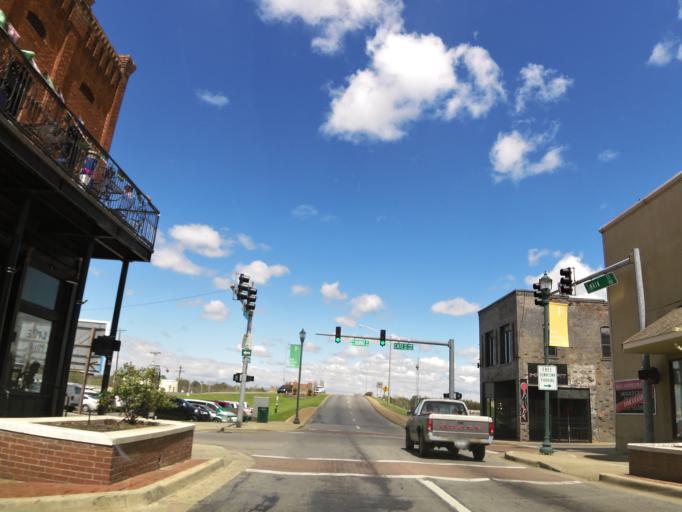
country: US
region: Arkansas
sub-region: Craighead County
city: Jonesboro
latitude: 35.8419
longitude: -90.7049
